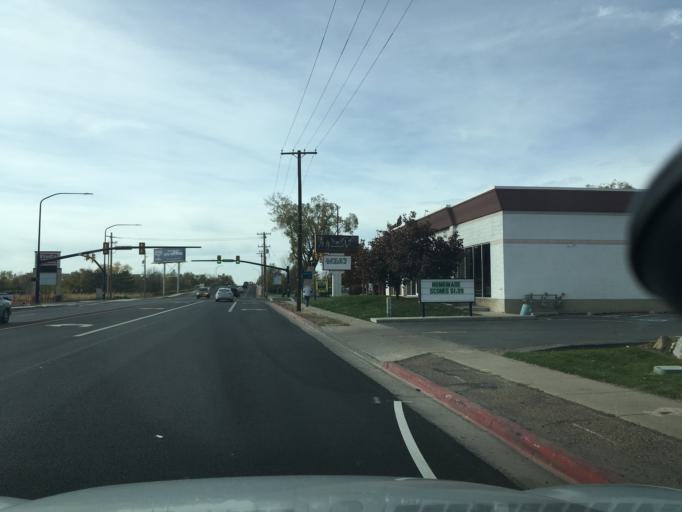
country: US
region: Utah
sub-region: Davis County
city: Layton
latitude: 41.0602
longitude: -111.9600
